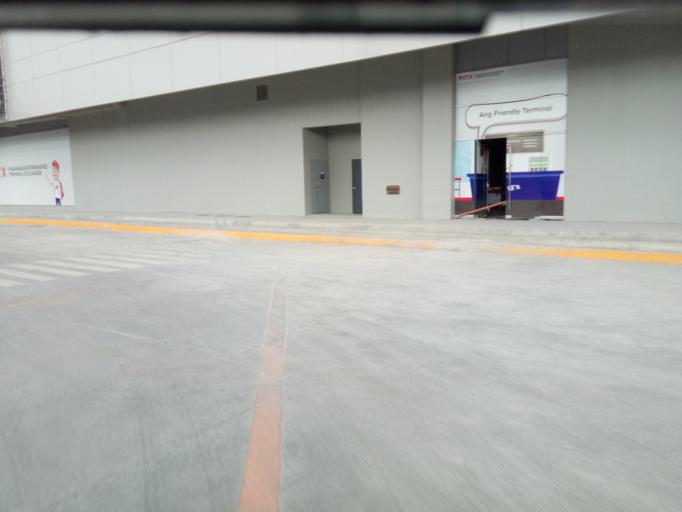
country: PH
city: Sambayanihan People's Village
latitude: 14.5106
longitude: 120.9911
